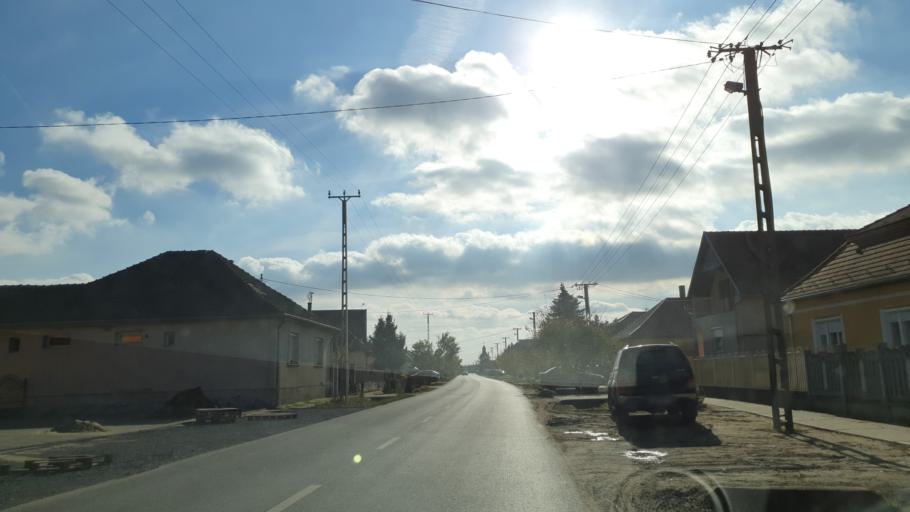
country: HU
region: Szabolcs-Szatmar-Bereg
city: Nyirkarasz
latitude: 48.1017
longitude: 22.0976
